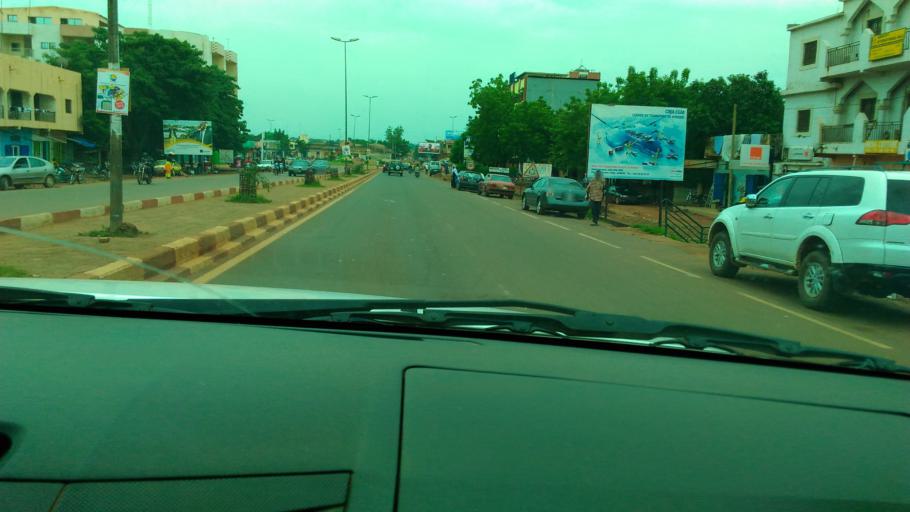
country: ML
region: Bamako
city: Bamako
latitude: 12.5829
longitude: -7.9917
